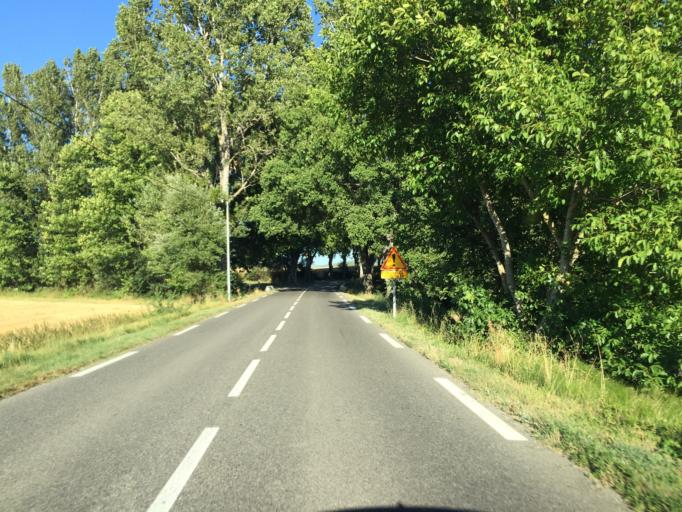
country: FR
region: Provence-Alpes-Cote d'Azur
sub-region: Departement des Alpes-de-Haute-Provence
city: Reillanne
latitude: 43.8602
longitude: 5.6248
